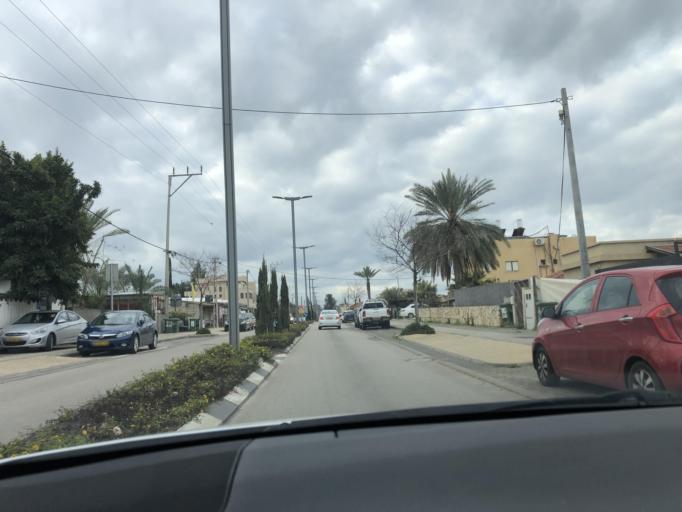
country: IL
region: Central District
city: Rosh Ha'Ayin
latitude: 32.0981
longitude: 34.9547
